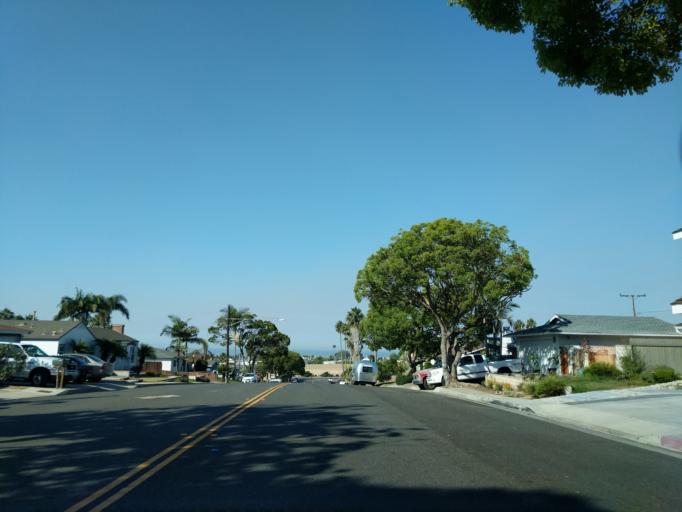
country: US
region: California
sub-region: Orange County
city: San Clemente
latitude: 33.4023
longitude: -117.5933
